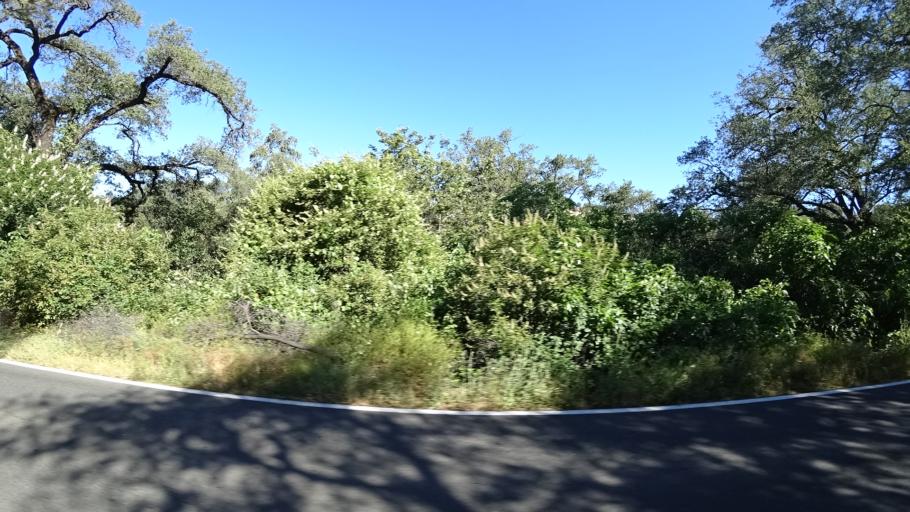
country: US
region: California
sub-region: Placer County
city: Newcastle
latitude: 38.8772
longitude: -121.1508
